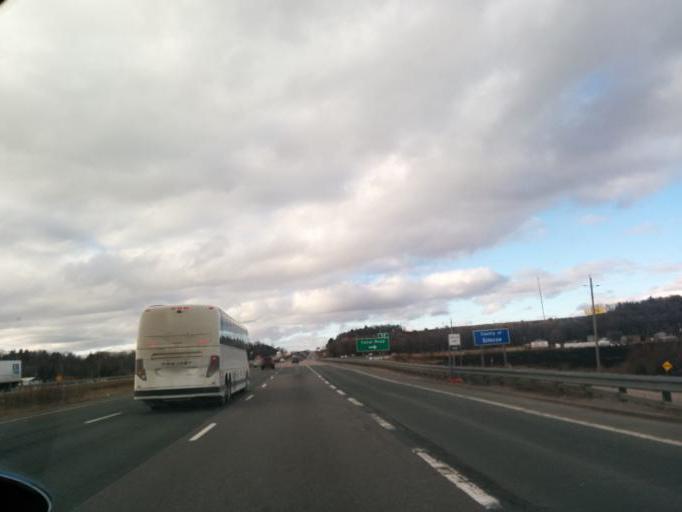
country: CA
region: Ontario
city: Bradford West Gwillimbury
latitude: 44.0486
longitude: -79.6058
